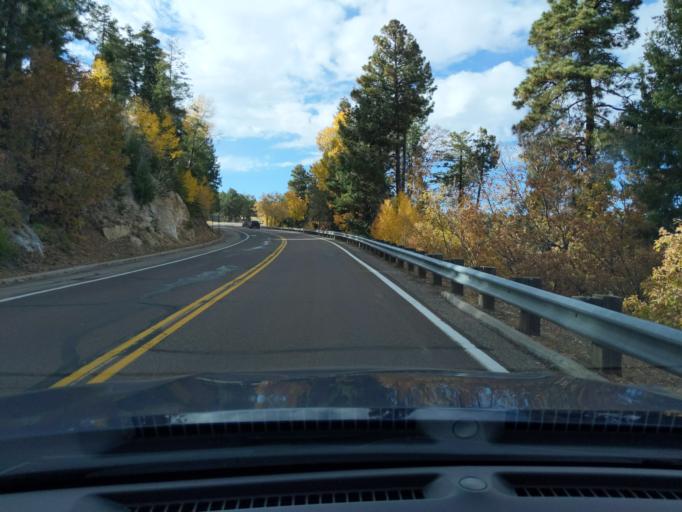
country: US
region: Arizona
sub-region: Pinal County
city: Oracle
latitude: 32.4321
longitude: -110.7485
